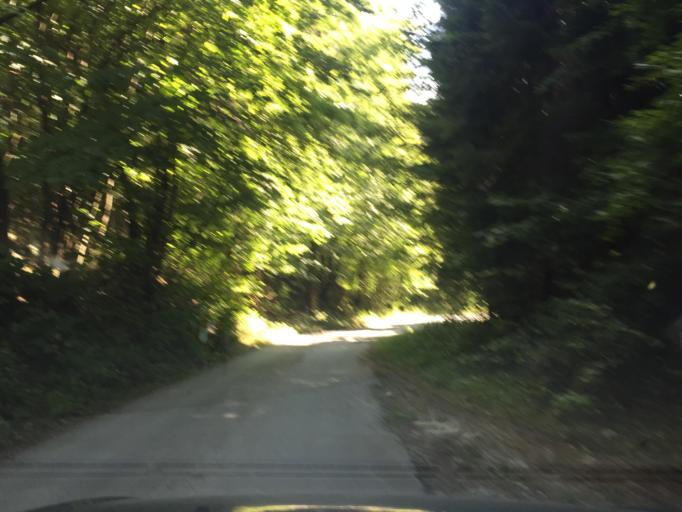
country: HR
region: Primorsko-Goranska
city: Klana
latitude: 45.4719
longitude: 14.4232
